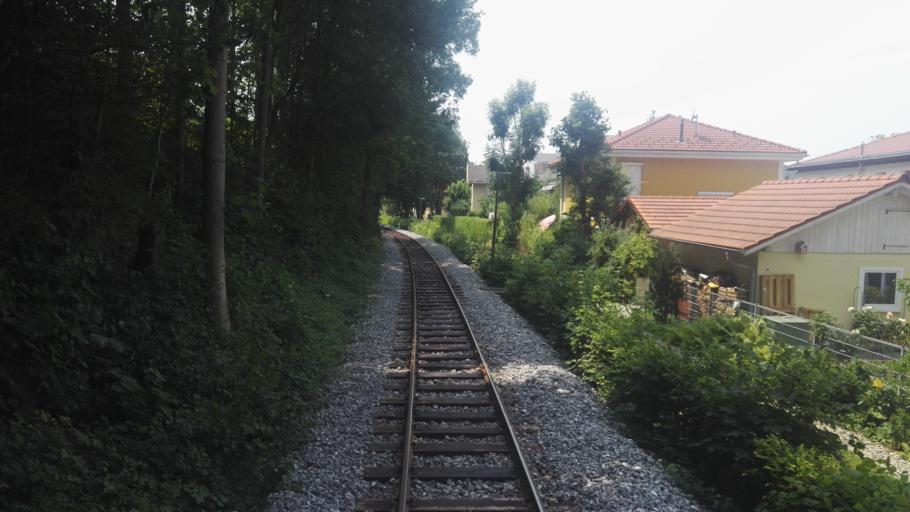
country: DE
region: Bavaria
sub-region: Upper Bavaria
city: Prien am Chiemsee
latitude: 47.8602
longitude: 12.3560
